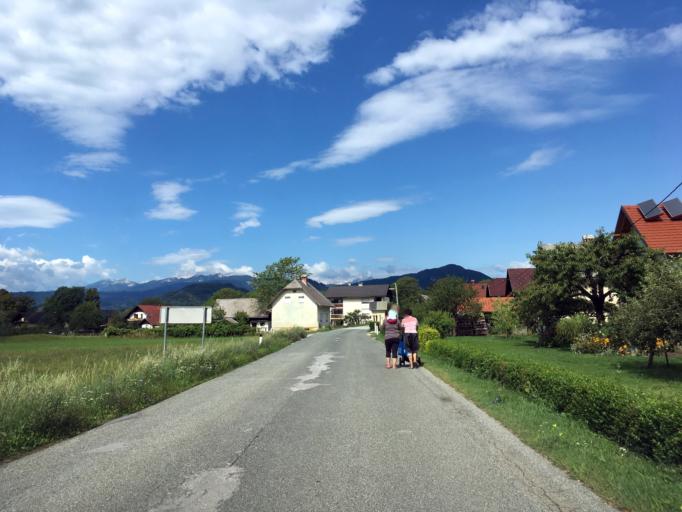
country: SI
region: Zirovnica
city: Zirovnica
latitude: 46.3964
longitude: 14.1507
